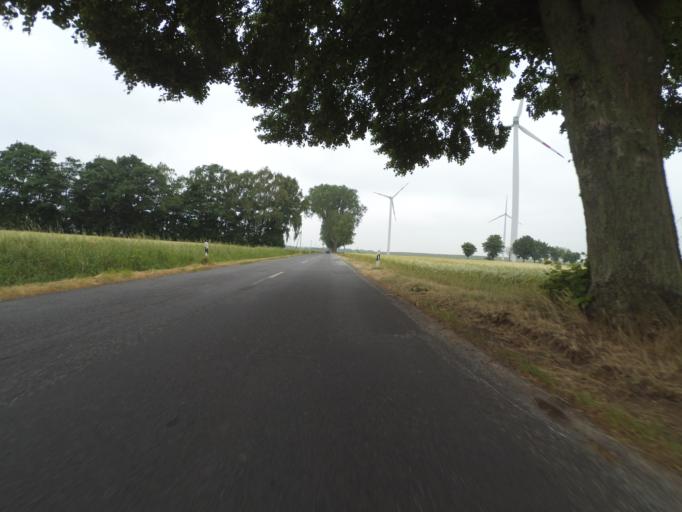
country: DE
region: Mecklenburg-Vorpommern
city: Plau am See
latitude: 53.4924
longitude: 12.2377
